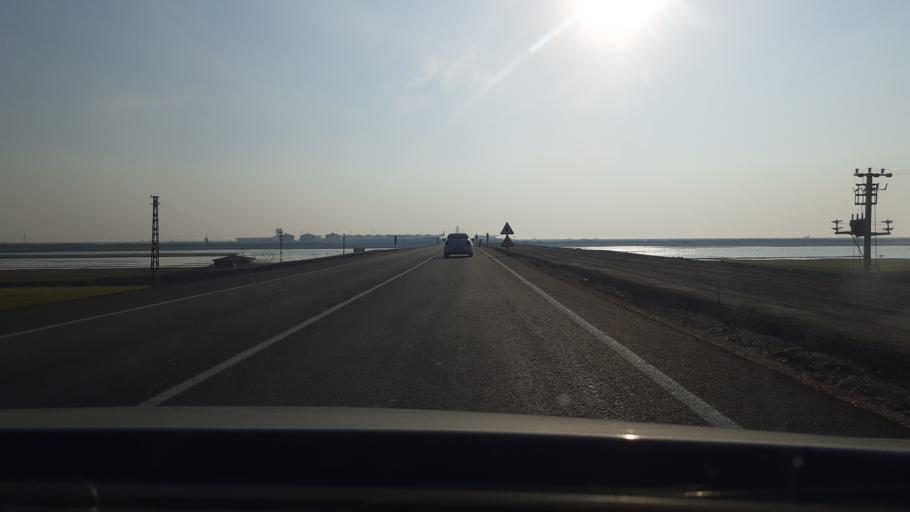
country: TR
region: Hatay
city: Serinyol
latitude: 36.3671
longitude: 36.2645
